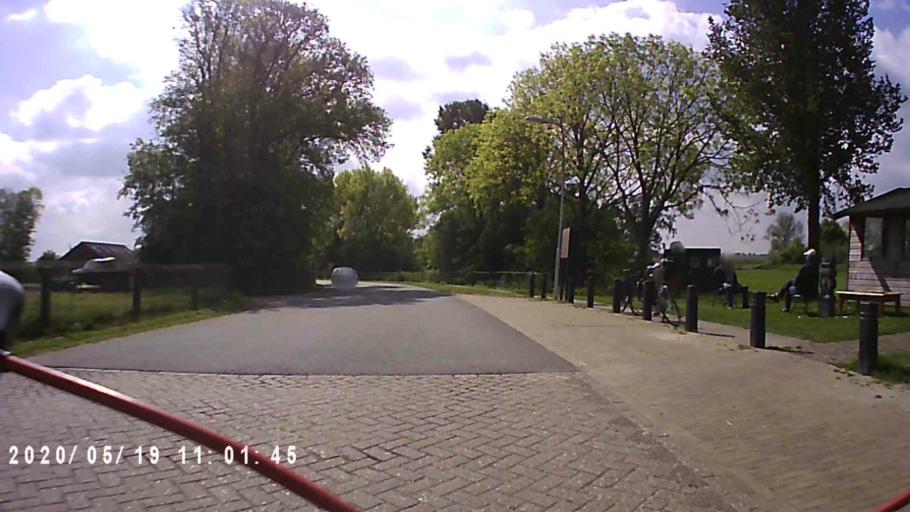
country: NL
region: Groningen
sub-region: Gemeente Zuidhorn
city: Grijpskerk
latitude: 53.3019
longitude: 6.2744
